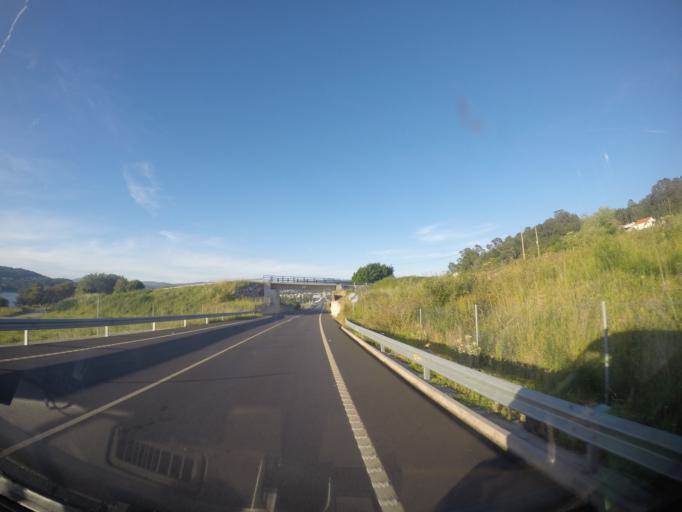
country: ES
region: Galicia
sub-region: Provincia da Coruna
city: Noia
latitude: 42.7872
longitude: -8.9156
